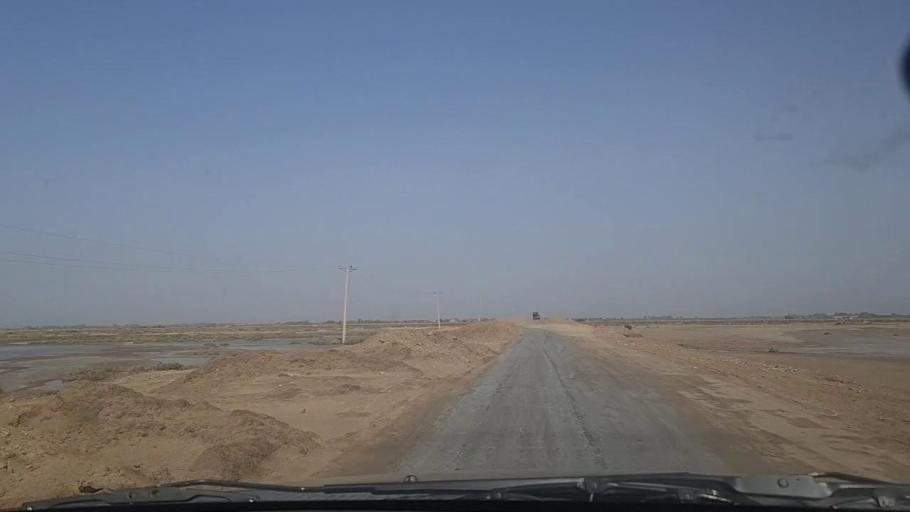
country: PK
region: Sindh
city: Keti Bandar
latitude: 24.1560
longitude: 67.5168
